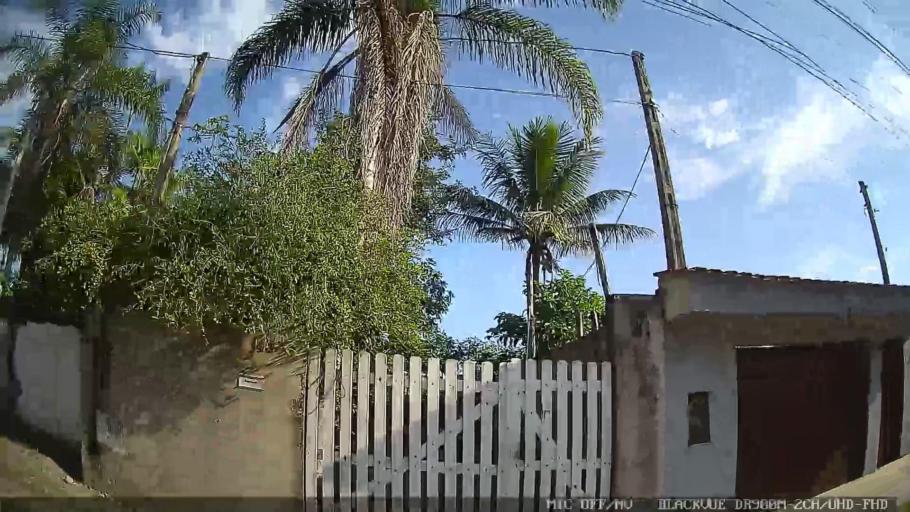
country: BR
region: Sao Paulo
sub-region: Itanhaem
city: Itanhaem
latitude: -24.1768
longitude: -46.8132
